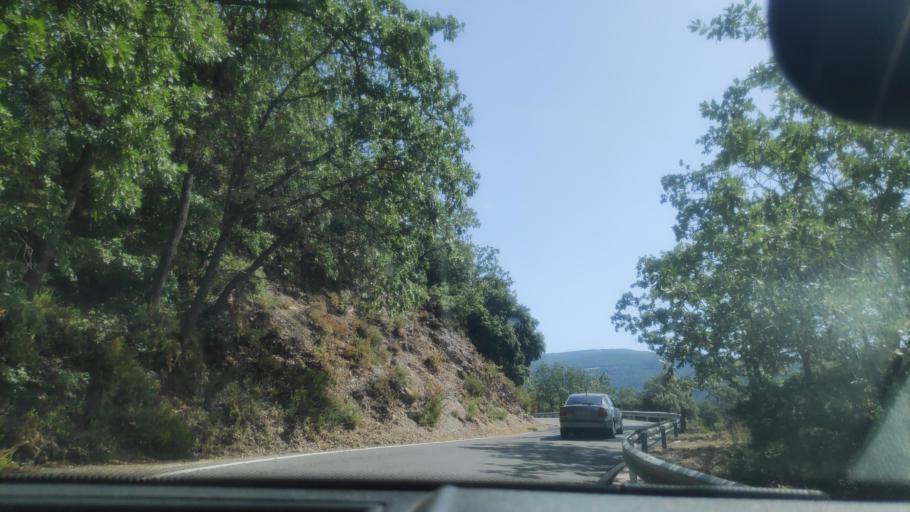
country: ES
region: Andalusia
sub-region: Provincia de Granada
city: Busquistar
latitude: 36.9422
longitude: -3.2867
